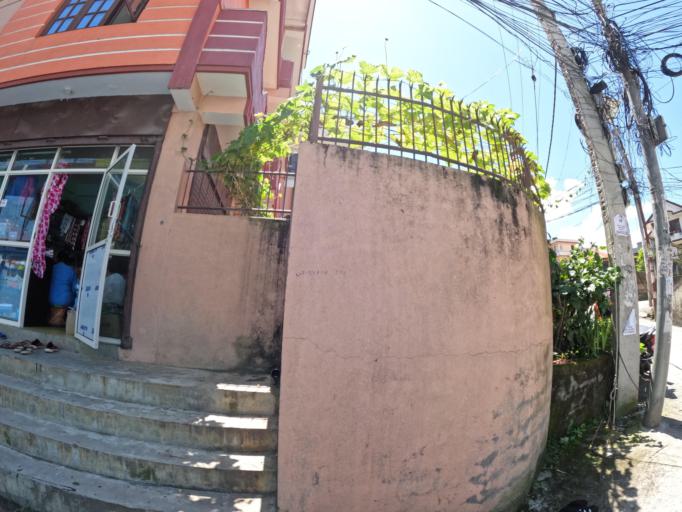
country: NP
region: Central Region
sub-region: Bagmati Zone
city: Kathmandu
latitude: 27.7453
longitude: 85.3255
